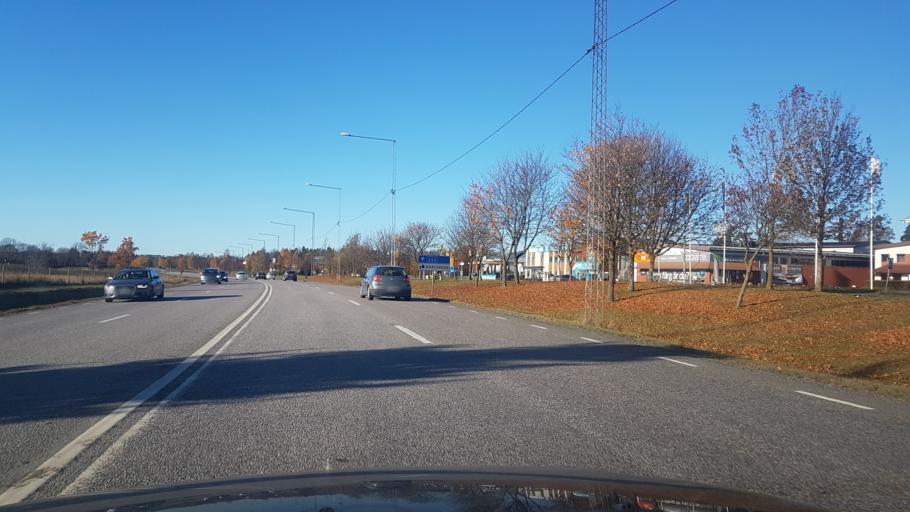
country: SE
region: Stockholm
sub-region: Sigtuna Kommun
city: Marsta
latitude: 59.6129
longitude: 17.8813
